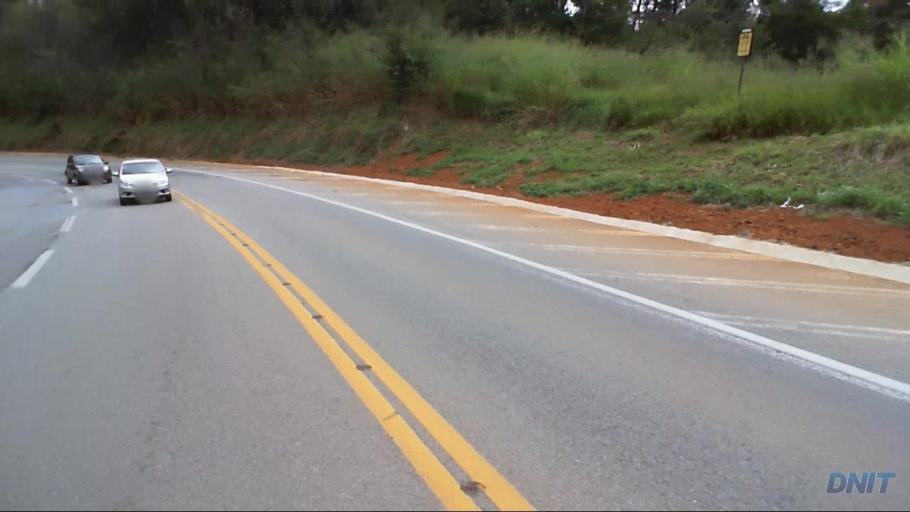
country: BR
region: Minas Gerais
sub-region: Joao Monlevade
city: Joao Monlevade
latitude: -19.8630
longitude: -43.1246
